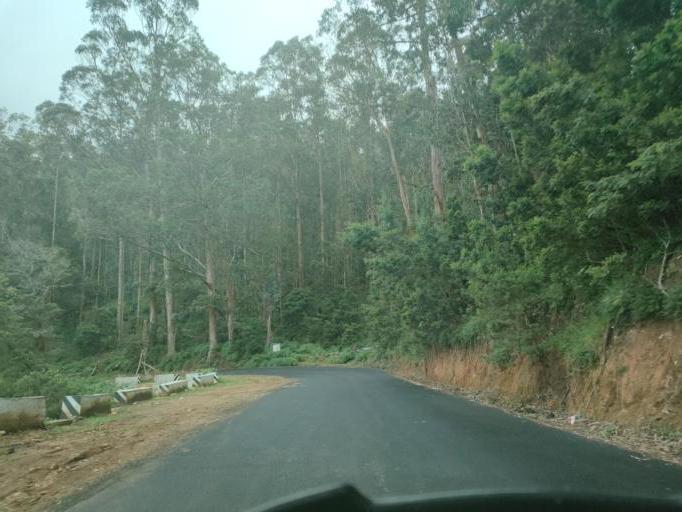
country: IN
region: Tamil Nadu
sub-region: Dindigul
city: Kodaikanal
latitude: 10.2433
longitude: 77.3629
